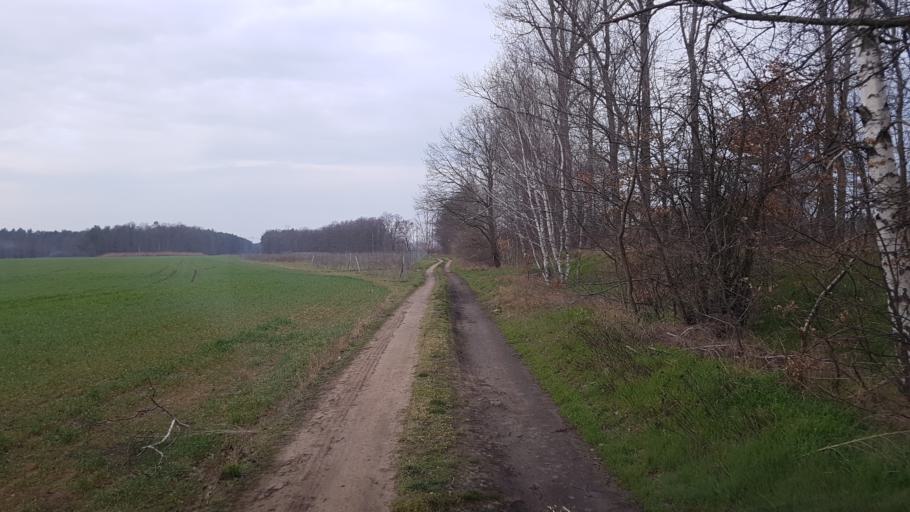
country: DE
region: Brandenburg
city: Falkenberg
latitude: 51.5843
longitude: 13.2848
